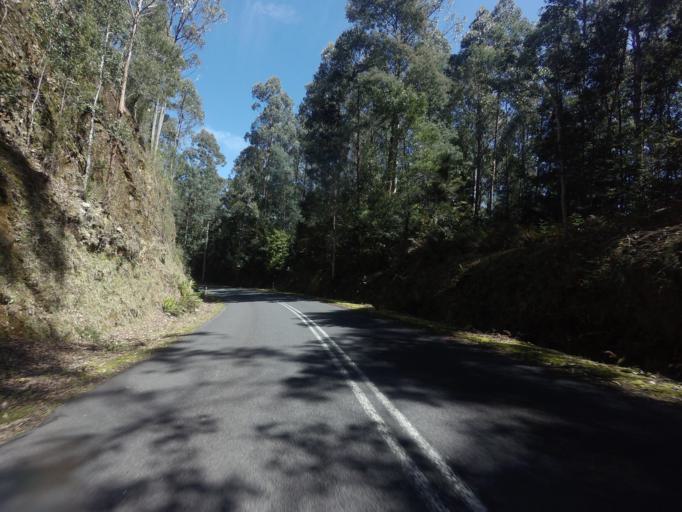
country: AU
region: Tasmania
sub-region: Huon Valley
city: Geeveston
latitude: -42.8260
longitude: 146.3246
